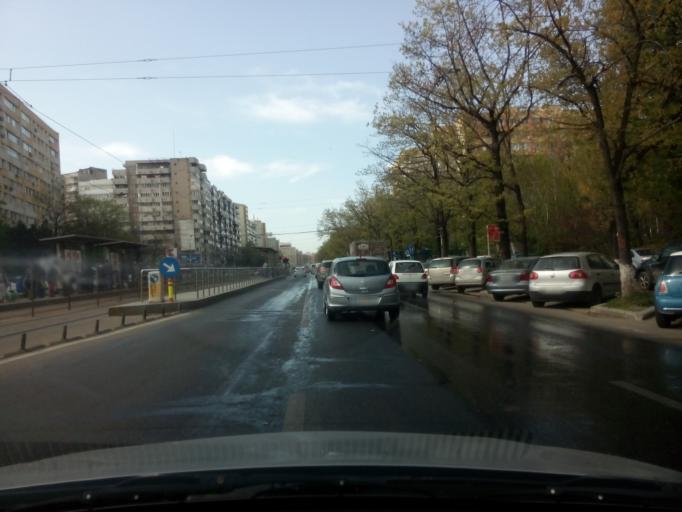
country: RO
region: Bucuresti
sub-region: Municipiul Bucuresti
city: Bucharest
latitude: 44.4546
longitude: 26.1283
